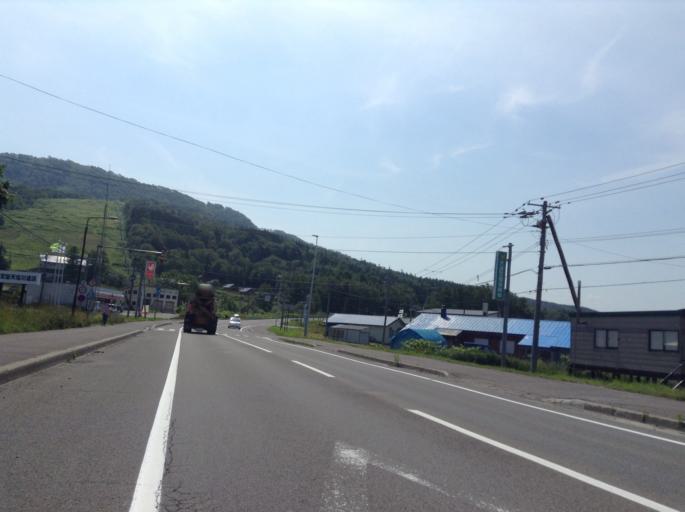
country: JP
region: Hokkaido
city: Nayoro
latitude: 44.7237
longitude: 142.2672
